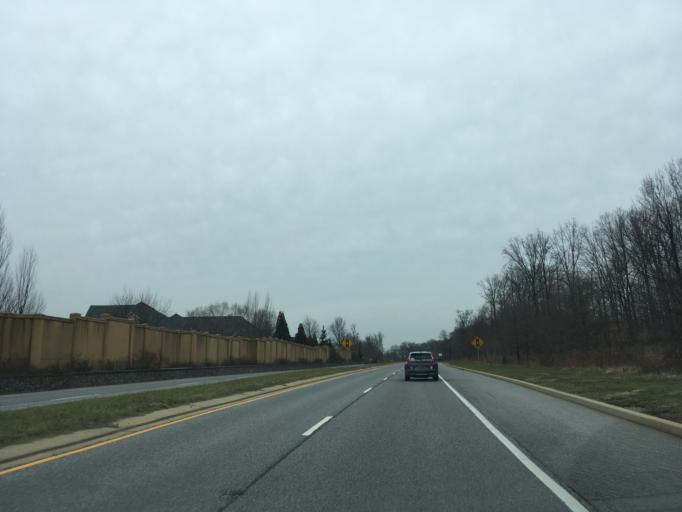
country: US
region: Delaware
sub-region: New Castle County
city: Wilmington
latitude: 39.7794
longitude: -75.5491
